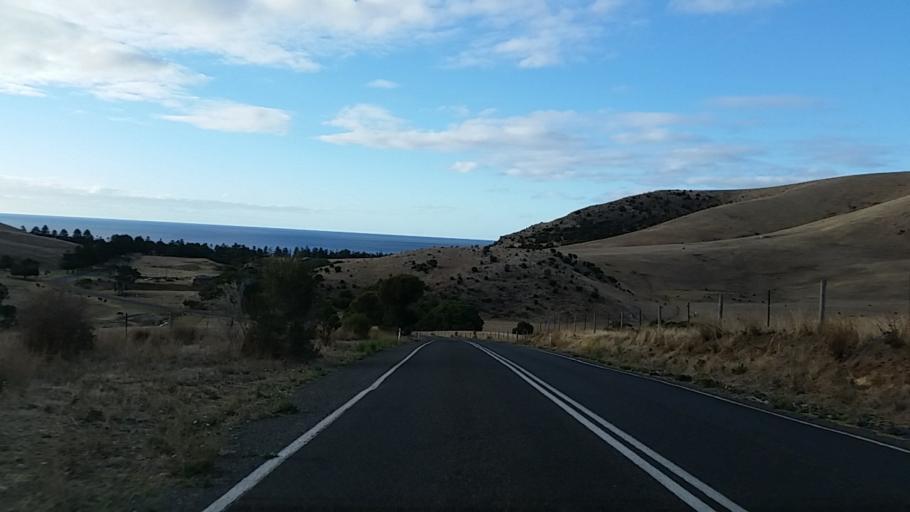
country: AU
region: South Australia
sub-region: Yankalilla
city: Normanville
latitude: -35.5360
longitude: 138.1944
